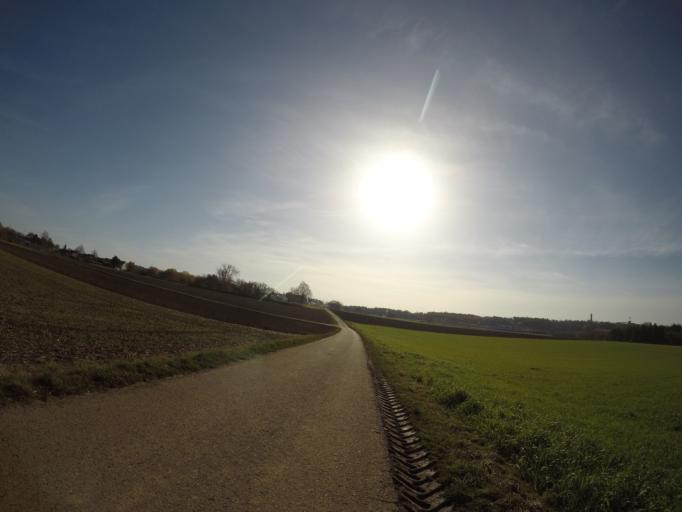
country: DE
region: Baden-Wuerttemberg
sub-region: Tuebingen Region
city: Dornstadt
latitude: 48.4344
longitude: 9.9621
